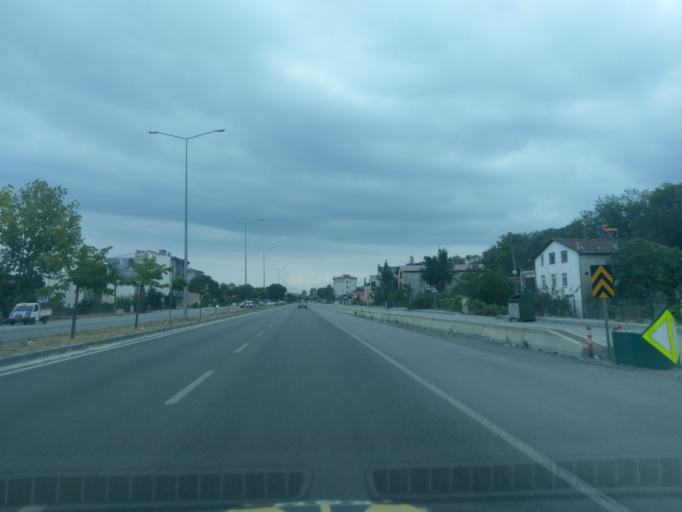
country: TR
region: Samsun
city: Taflan
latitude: 41.3990
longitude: 36.1936
